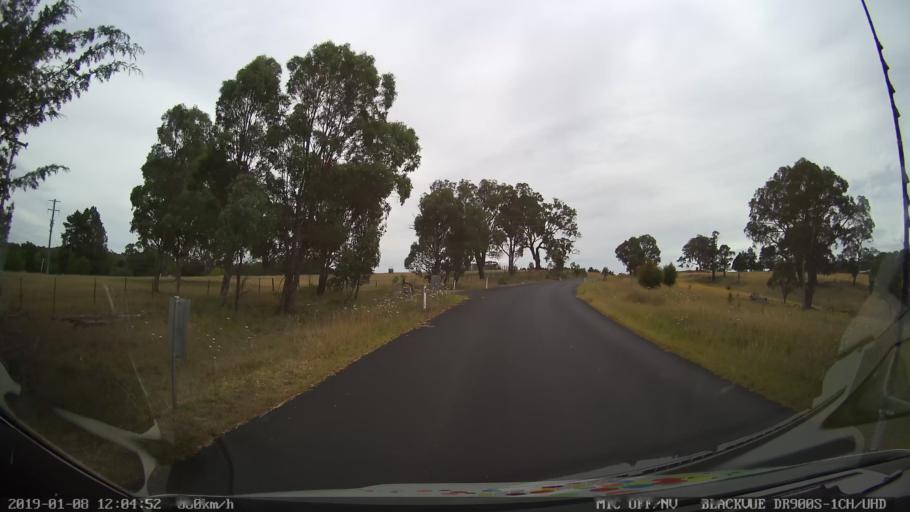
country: AU
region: New South Wales
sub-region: Armidale Dumaresq
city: Armidale
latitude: -30.4393
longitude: 151.5902
